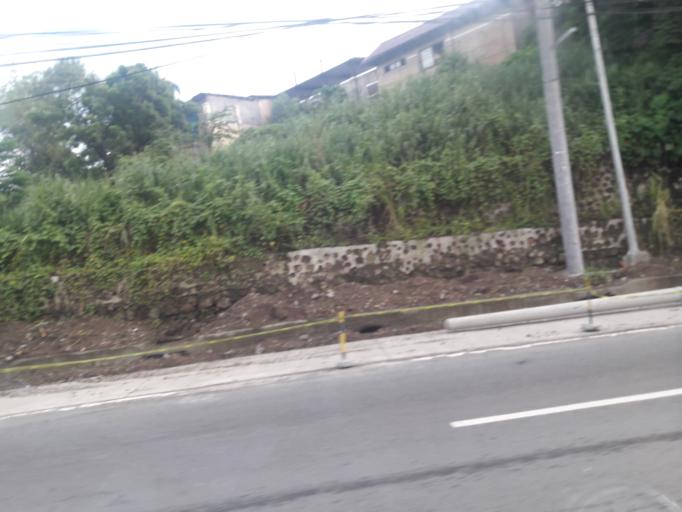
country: PH
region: Calabarzon
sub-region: Province of Cavite
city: Carmona
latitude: 14.3089
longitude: 121.0324
